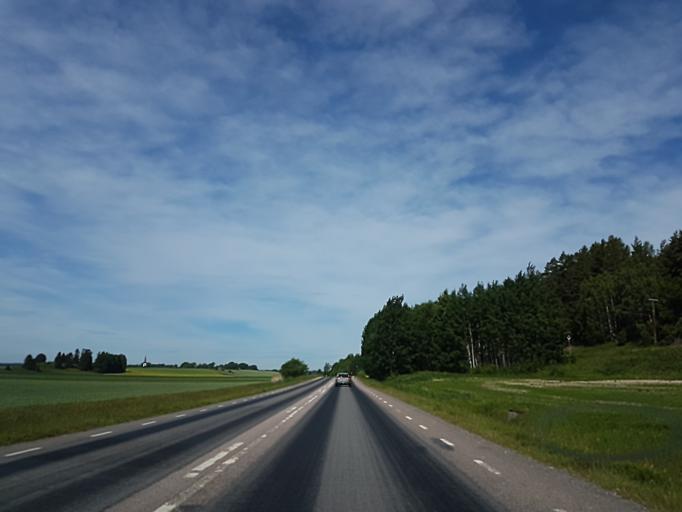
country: SE
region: Soedermanland
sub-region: Nykopings Kommun
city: Stigtomta
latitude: 58.7429
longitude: 16.7689
